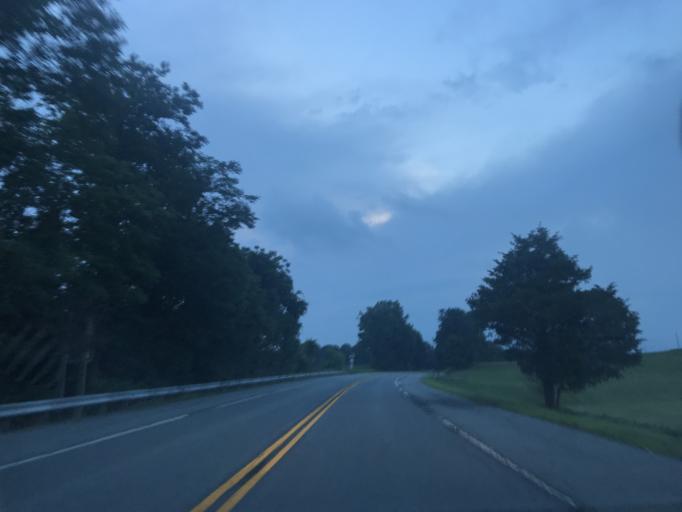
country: US
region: Maryland
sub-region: Cecil County
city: Rising Sun
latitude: 39.6971
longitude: -76.0810
